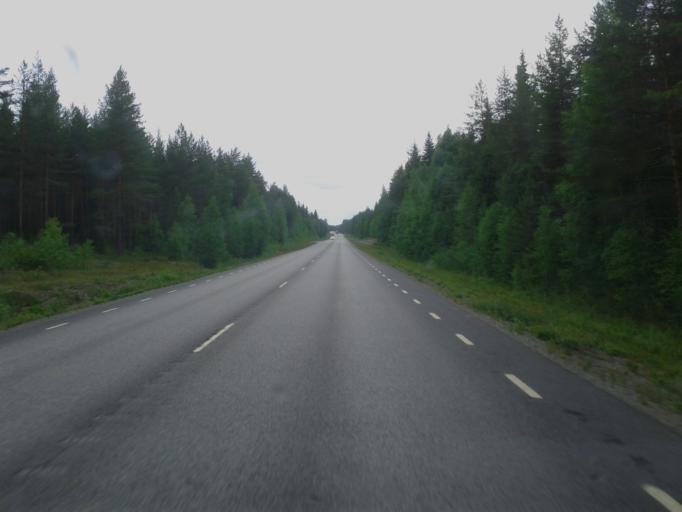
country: SE
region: Vaesterbotten
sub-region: Skelleftea Kommun
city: Langsele
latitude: 64.9407
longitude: 19.9345
